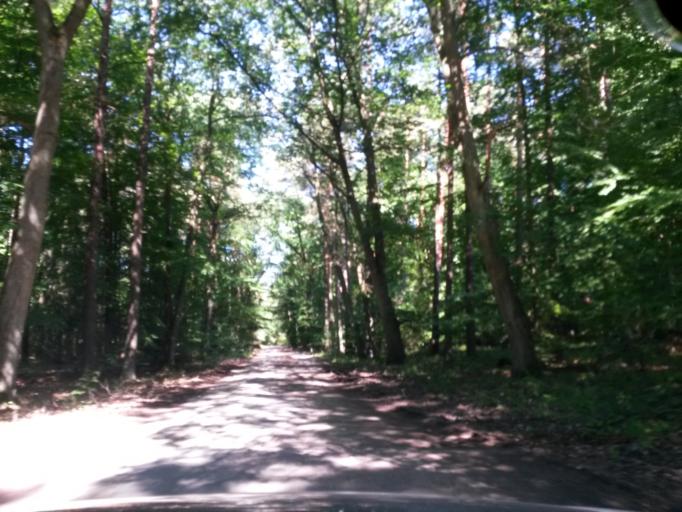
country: DE
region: Brandenburg
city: Templin
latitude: 53.2229
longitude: 13.4550
